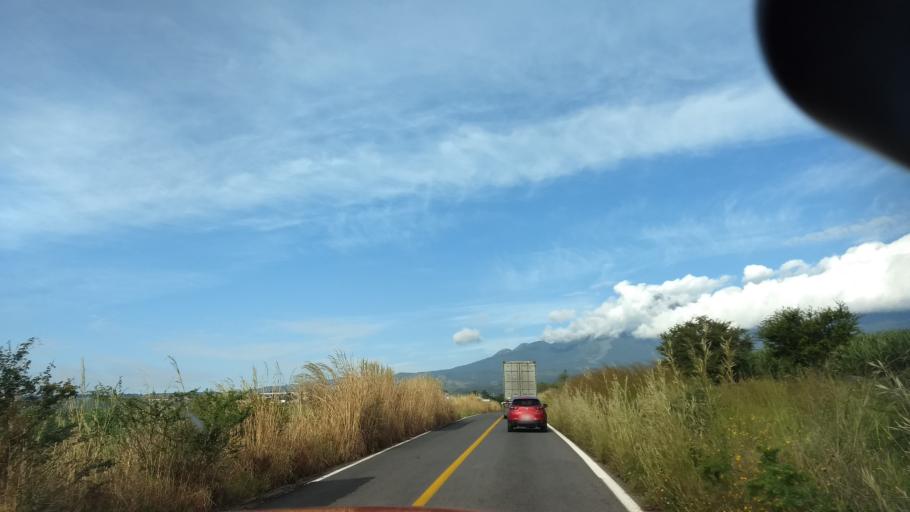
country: MX
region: Jalisco
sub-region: Tonila
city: San Marcos
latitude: 19.4362
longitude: -103.5038
